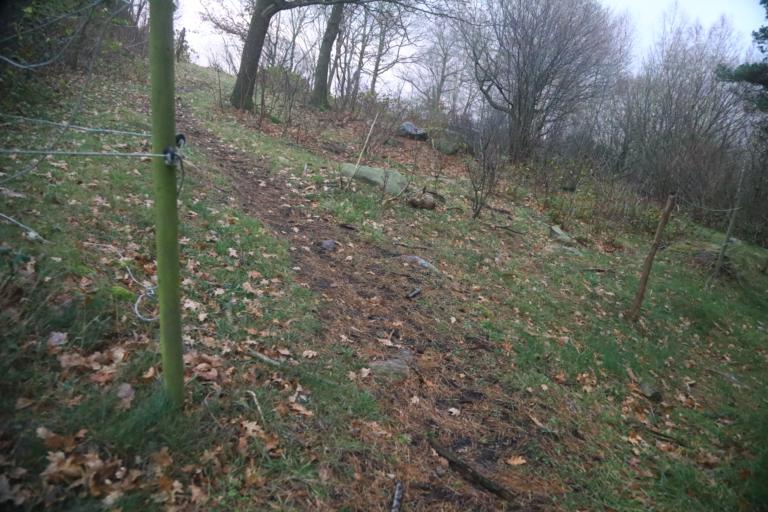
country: SE
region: Halland
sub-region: Varbergs Kommun
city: Traslovslage
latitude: 57.1095
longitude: 12.3275
